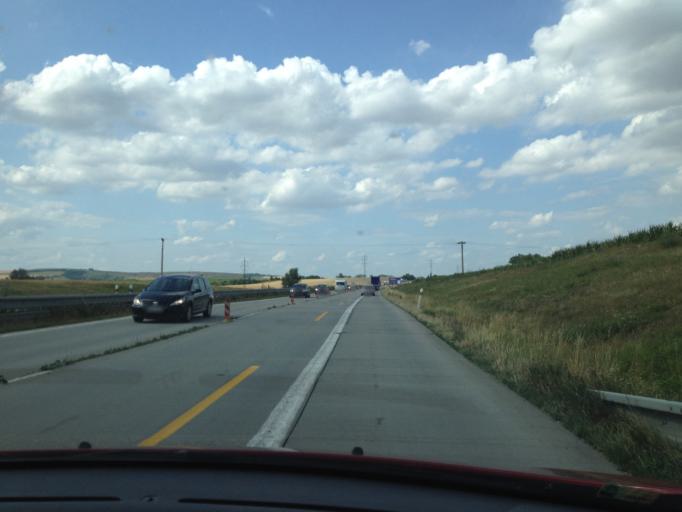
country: CZ
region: South Moravian
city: Velke Nemcice
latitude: 48.9963
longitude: 16.6889
